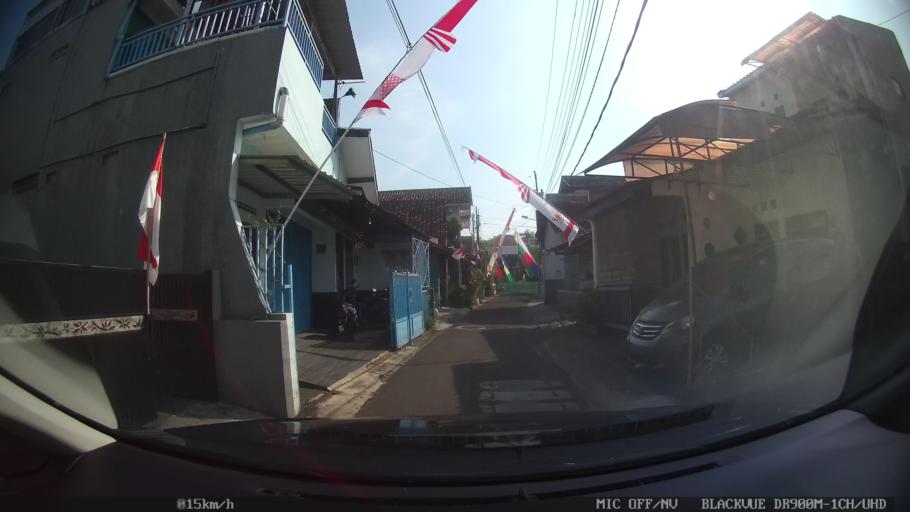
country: ID
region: Daerah Istimewa Yogyakarta
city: Yogyakarta
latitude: -7.7862
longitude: 110.3538
